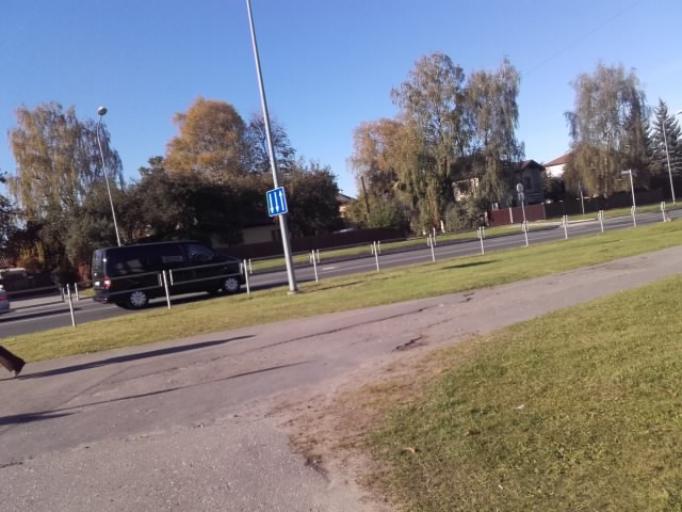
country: LV
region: Riga
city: Riga
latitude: 56.9410
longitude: 24.1956
